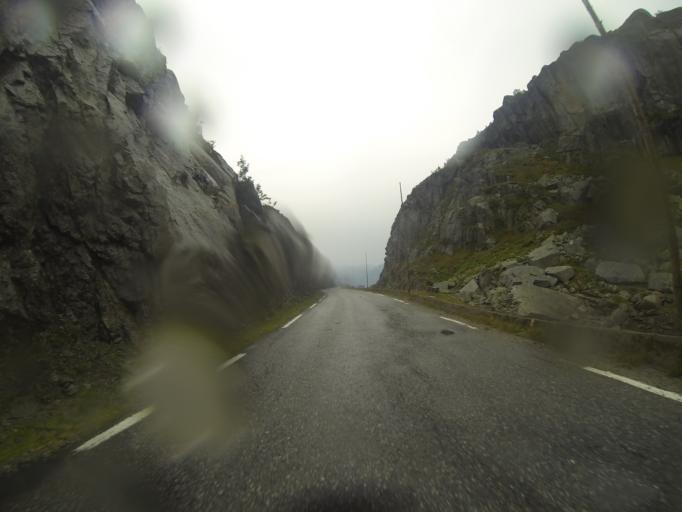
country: NO
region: Hordaland
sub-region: Odda
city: Odda
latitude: 59.7779
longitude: 6.7512
